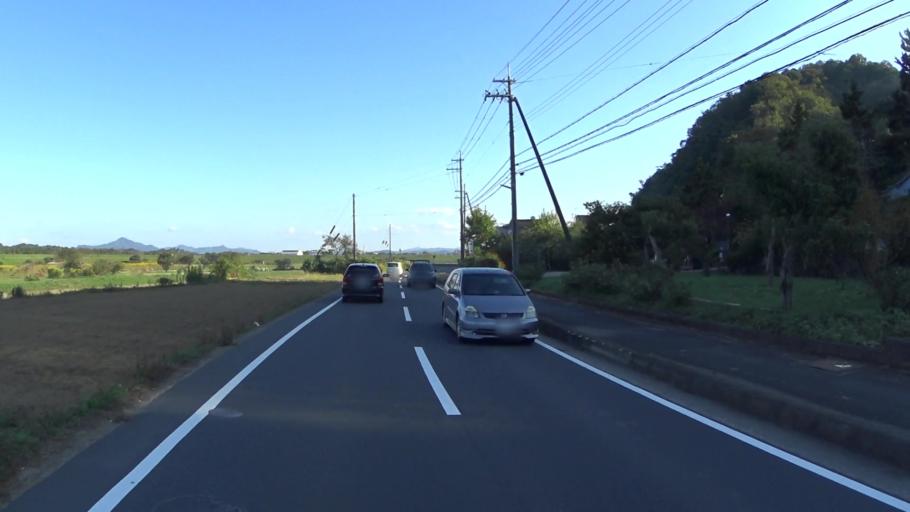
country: JP
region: Kyoto
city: Fukuchiyama
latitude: 35.3192
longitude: 135.1083
